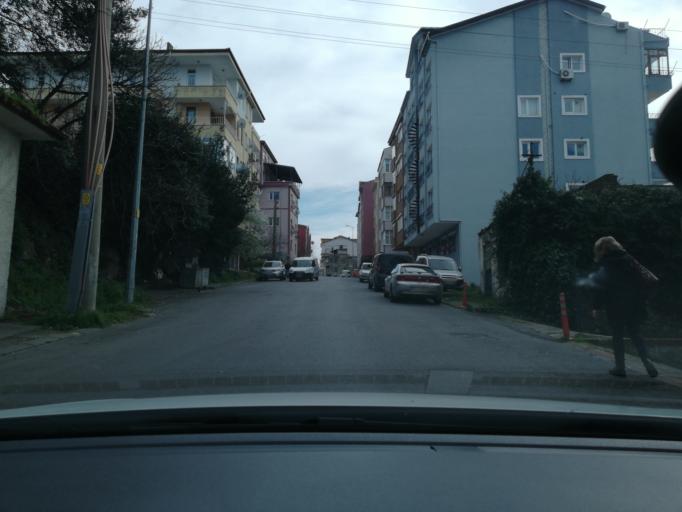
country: TR
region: Zonguldak
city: Eregli
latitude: 41.2846
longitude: 31.4162
